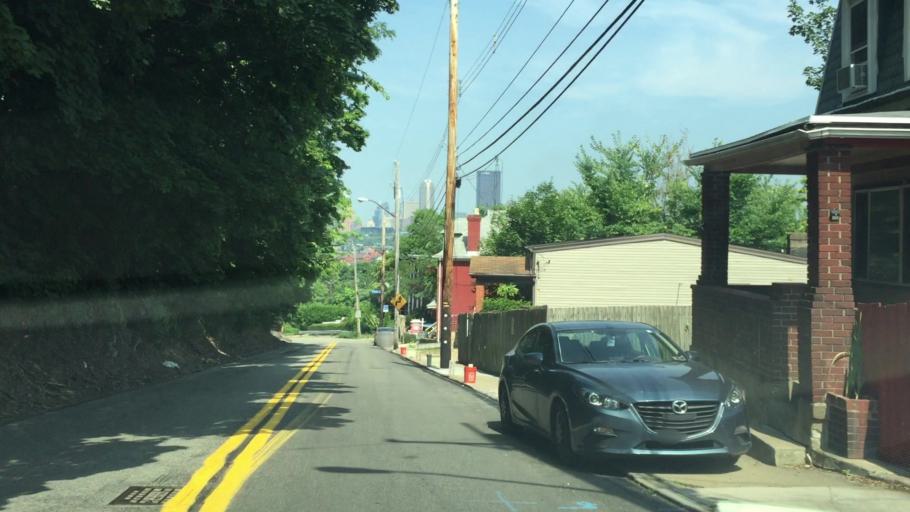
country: US
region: Pennsylvania
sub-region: Allegheny County
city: Mount Oliver
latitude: 40.4225
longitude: -79.9660
